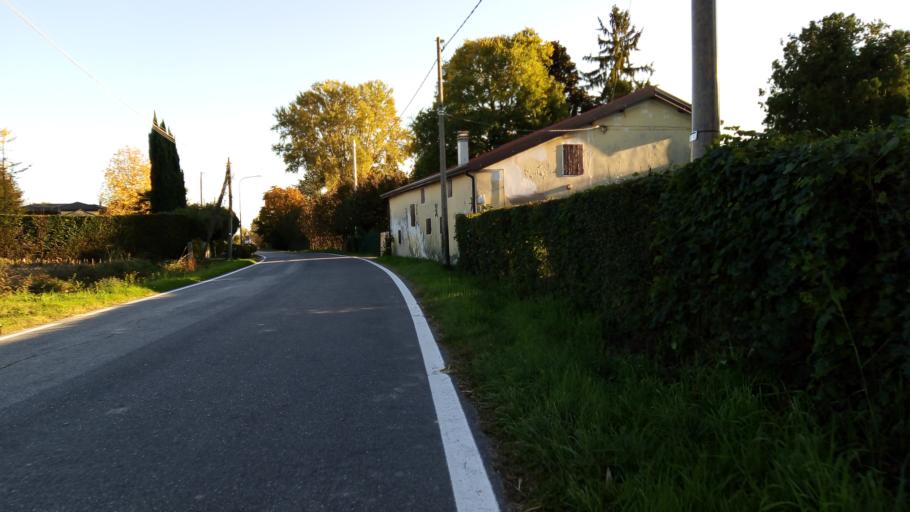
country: IT
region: Veneto
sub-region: Provincia di Padova
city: Abano Terme
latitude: 45.3532
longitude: 11.7995
